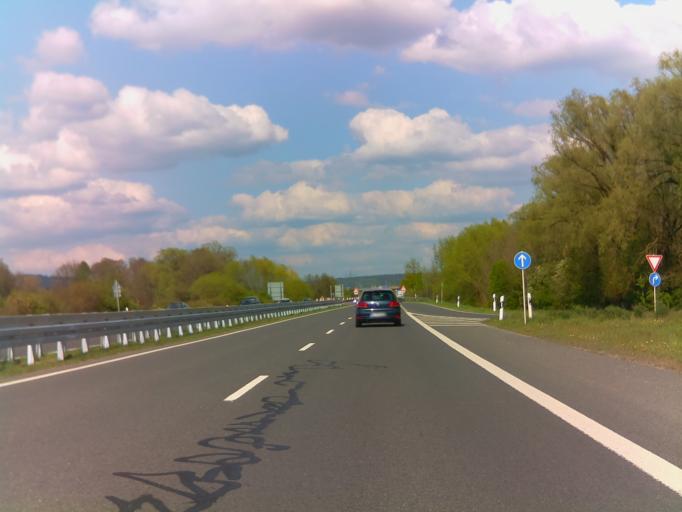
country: DE
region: Bavaria
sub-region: Upper Franconia
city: Coburg
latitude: 50.2799
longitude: 10.9626
